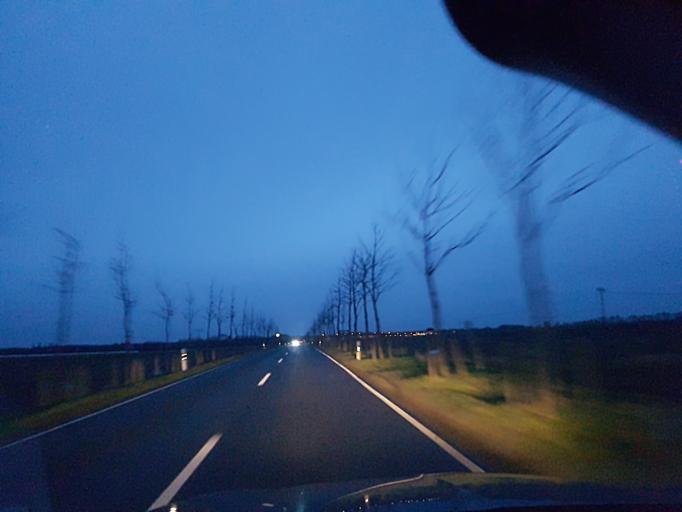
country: DE
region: Brandenburg
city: Doberlug-Kirchhain
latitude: 51.6166
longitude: 13.5780
